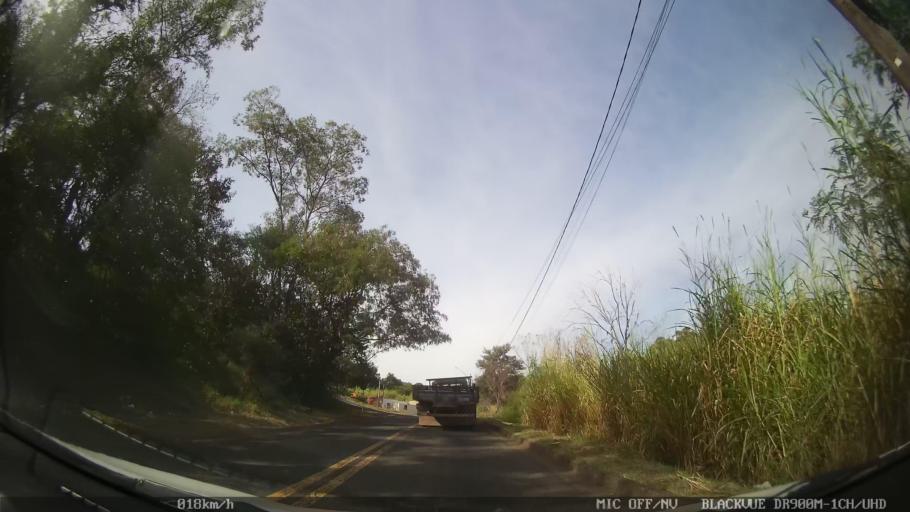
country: BR
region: Sao Paulo
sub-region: Piracicaba
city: Piracicaba
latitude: -22.7615
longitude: -47.5996
